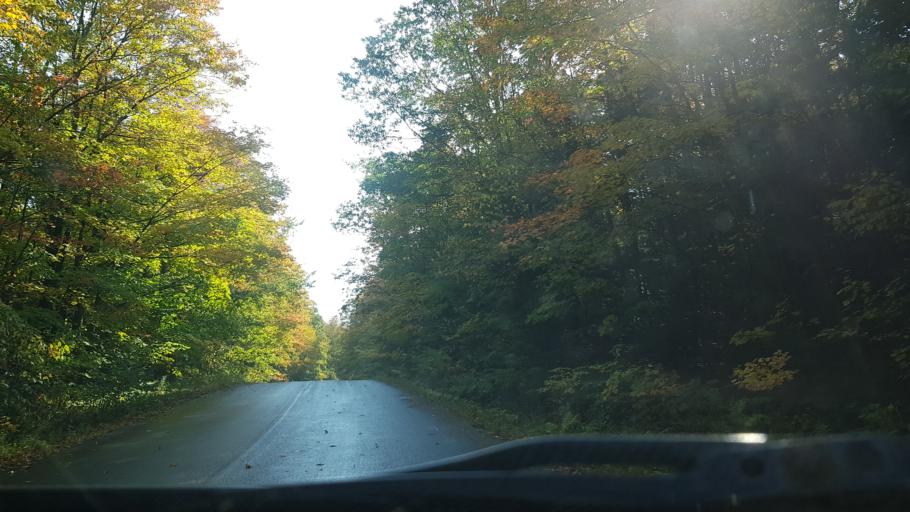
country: CA
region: Ontario
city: Bracebridge
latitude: 44.9570
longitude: -79.2488
